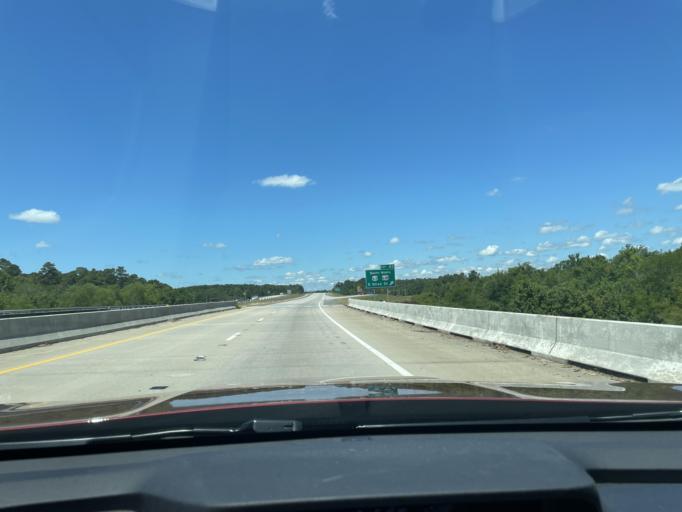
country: US
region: Arkansas
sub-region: Jefferson County
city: Pine Bluff
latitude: 34.1710
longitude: -92.0012
